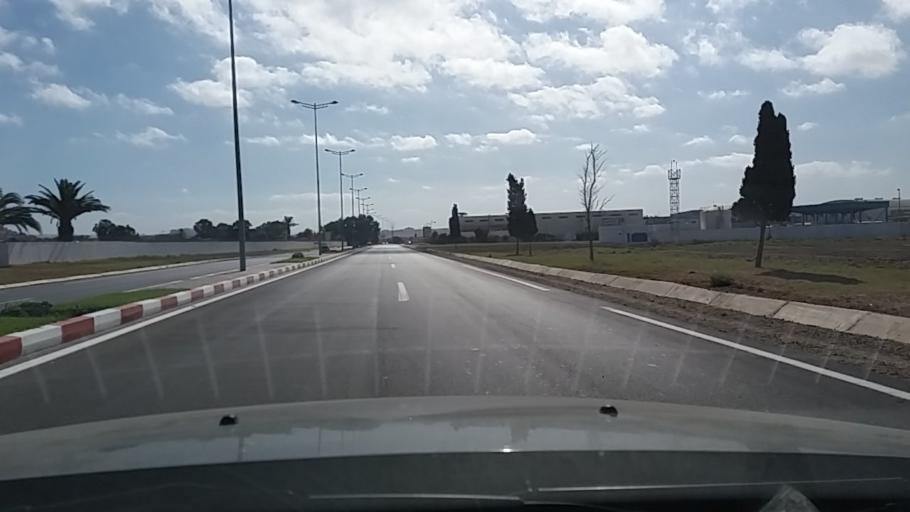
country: MA
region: Tanger-Tetouan
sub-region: Tanger-Assilah
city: Boukhalef
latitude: 35.7273
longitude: -5.9048
